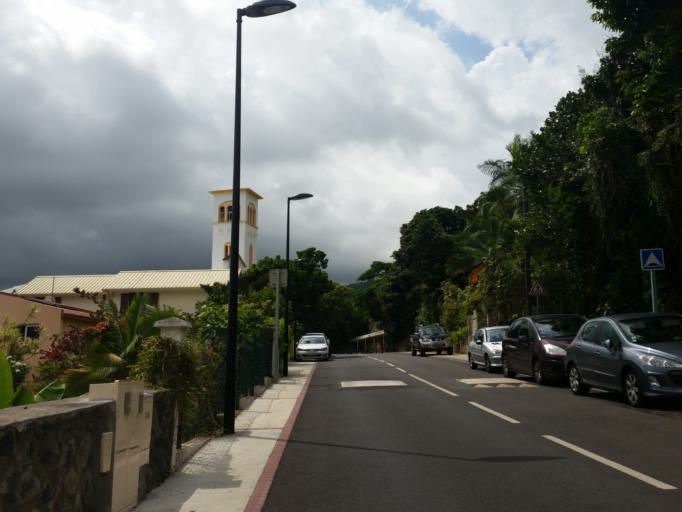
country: RE
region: Reunion
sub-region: Reunion
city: L'Entre-Deux
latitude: -21.2503
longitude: 55.4723
